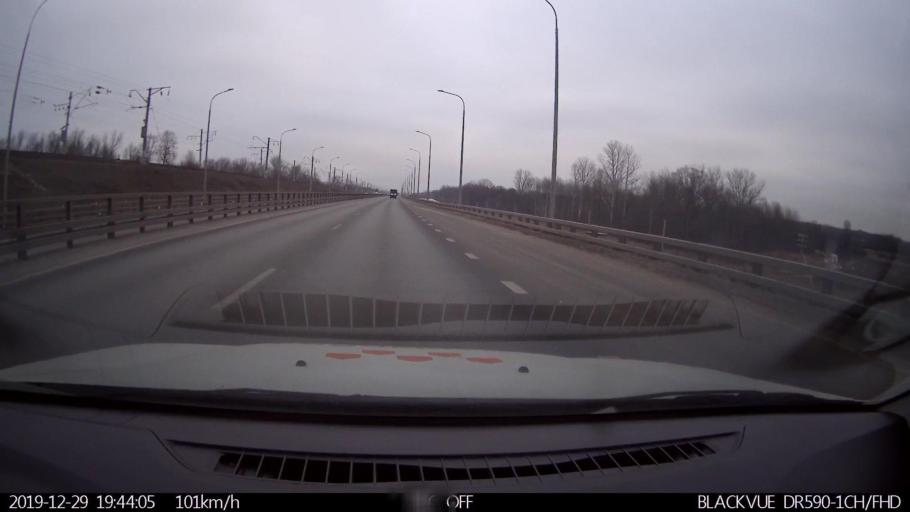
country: RU
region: Nizjnij Novgorod
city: Neklyudovo
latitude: 56.3711
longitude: 43.9445
